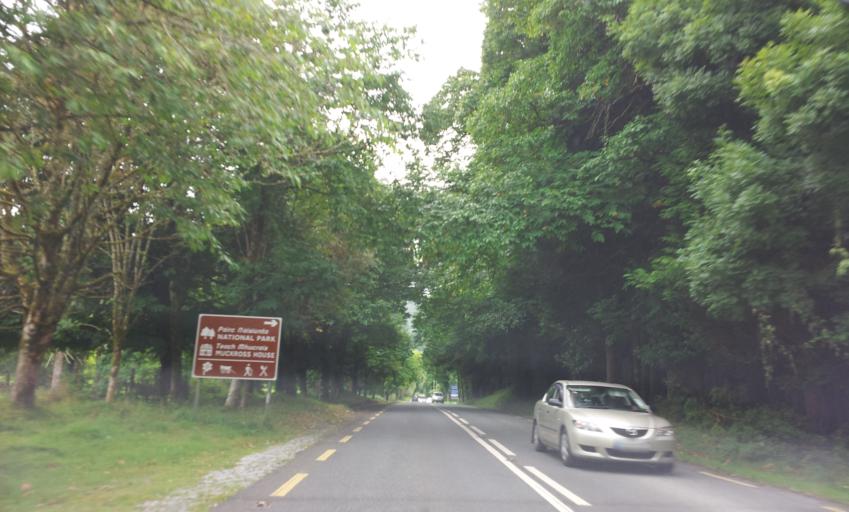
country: IE
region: Munster
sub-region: Ciarrai
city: Cill Airne
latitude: 52.0196
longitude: -9.4938
